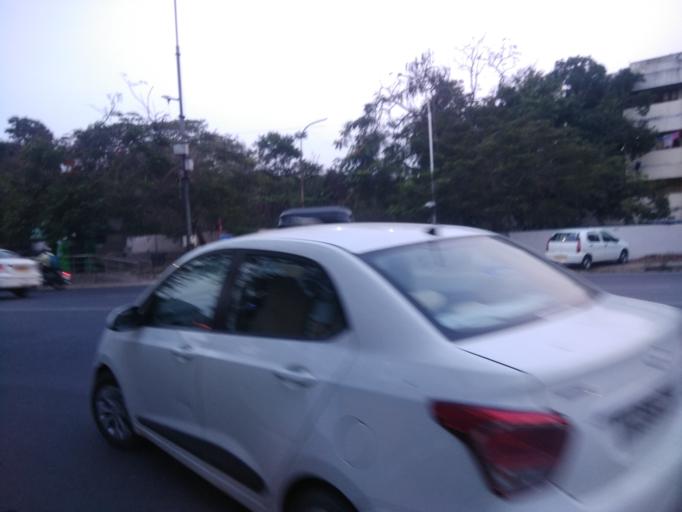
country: IN
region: Tamil Nadu
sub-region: Kancheepuram
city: Alandur
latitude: 13.0125
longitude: 80.2269
